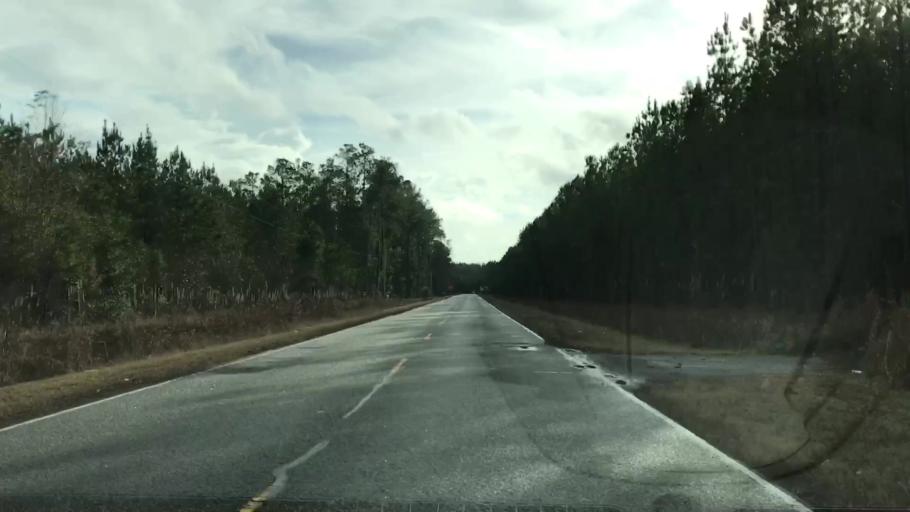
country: US
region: South Carolina
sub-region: Williamsburg County
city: Andrews
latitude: 33.4259
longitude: -79.5950
